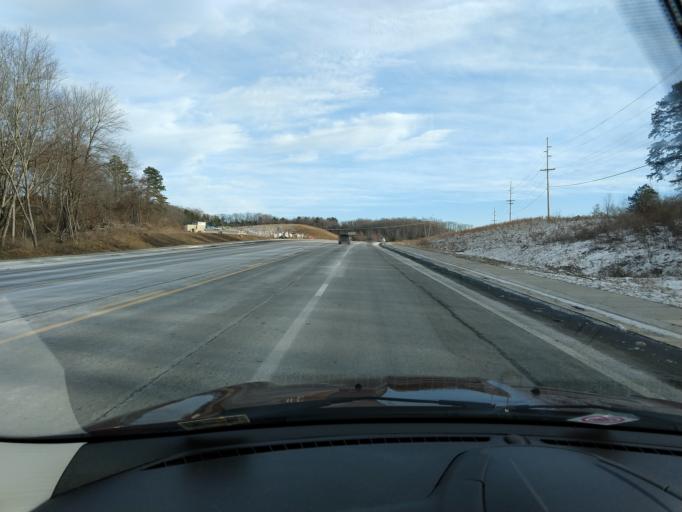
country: US
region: West Virginia
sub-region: Raleigh County
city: Stanaford
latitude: 37.8049
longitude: -81.1733
